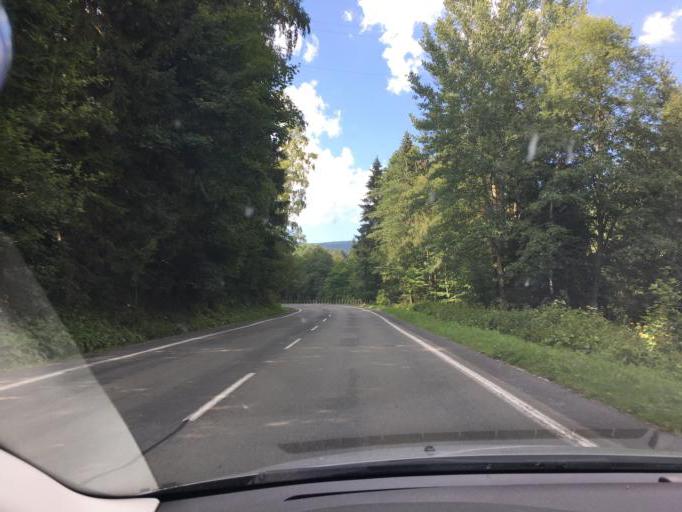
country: CZ
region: Kralovehradecky
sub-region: Okres Trutnov
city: Spindleruv Mlyn
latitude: 50.7043
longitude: 15.5833
